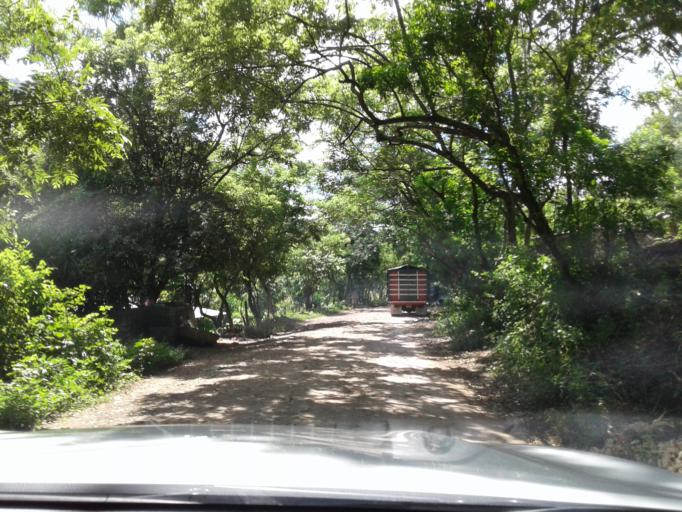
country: NI
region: Matagalpa
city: Terrabona
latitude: 12.8408
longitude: -86.0014
